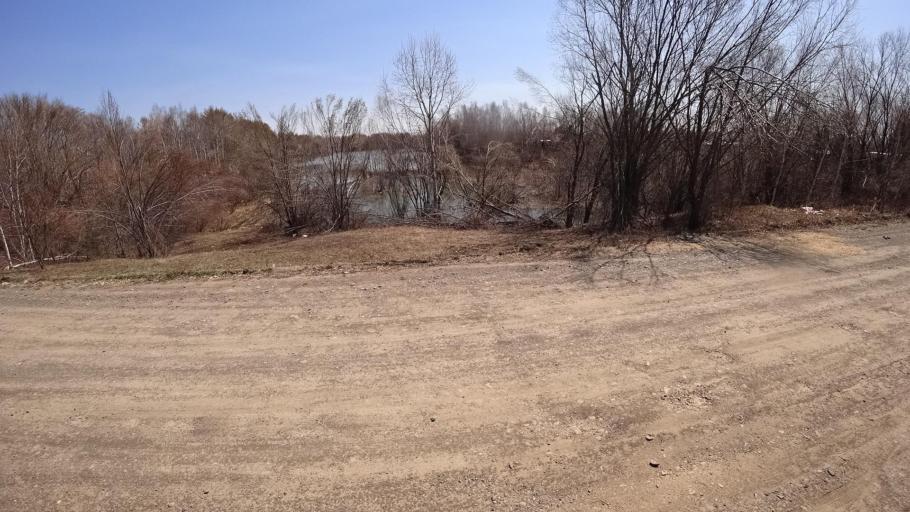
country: RU
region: Khabarovsk Krai
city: Khurba
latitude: 50.4155
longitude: 136.8624
